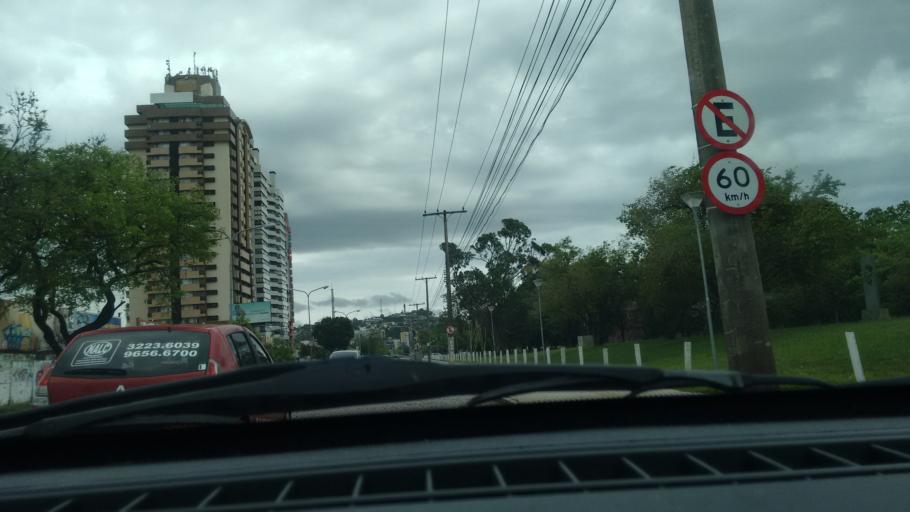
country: BR
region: Rio Grande do Sul
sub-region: Porto Alegre
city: Porto Alegre
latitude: -30.0535
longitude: -51.2301
